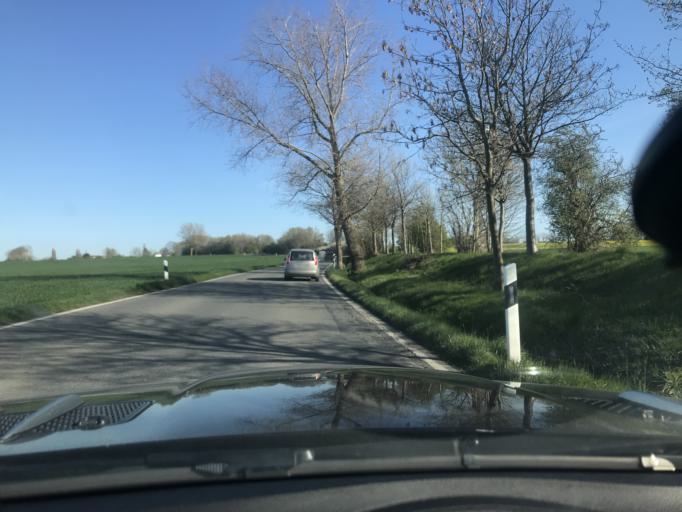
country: DE
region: Schleswig-Holstein
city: Fehmarn
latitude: 54.4564
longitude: 11.1362
